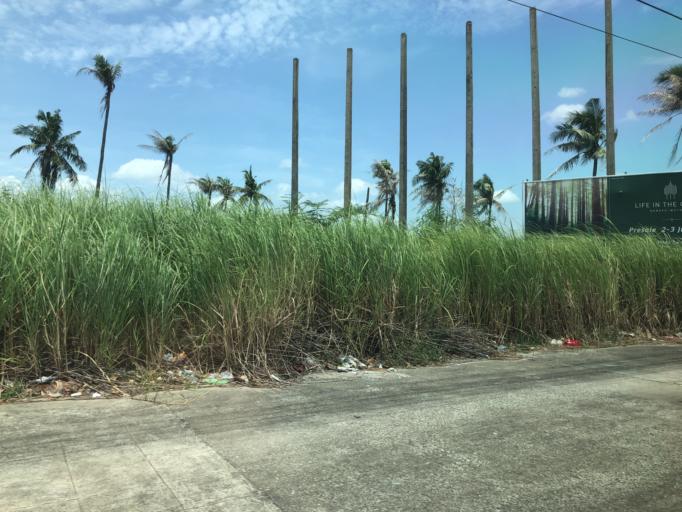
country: TH
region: Chon Buri
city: Bang Lamung
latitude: 13.0330
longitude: 100.9288
